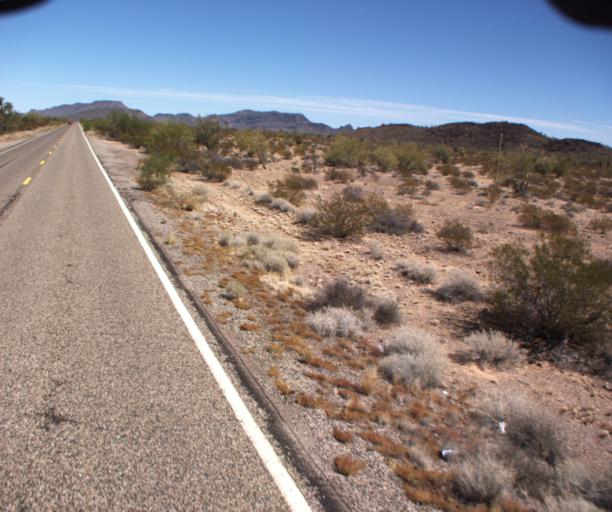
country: US
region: Arizona
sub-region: Pima County
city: Ajo
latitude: 32.2299
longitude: -112.7538
